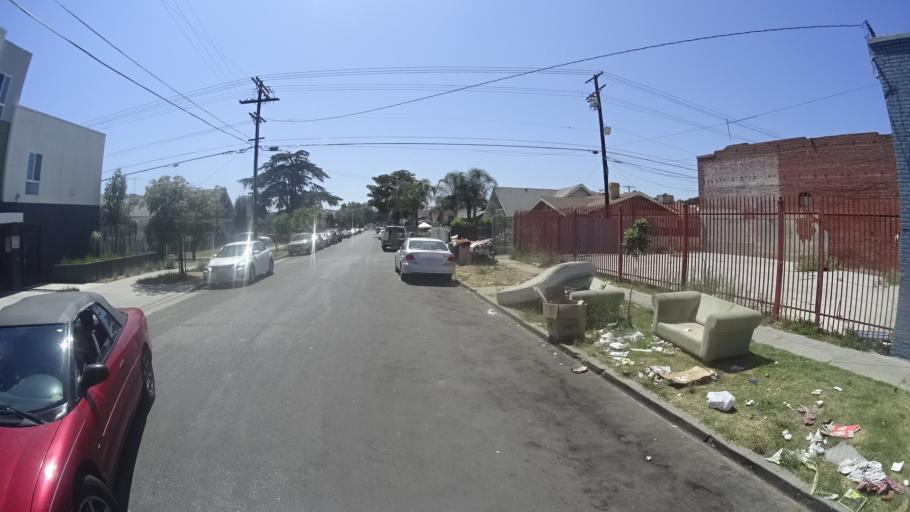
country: US
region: California
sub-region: Los Angeles County
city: View Park-Windsor Hills
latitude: 33.9988
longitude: -118.2918
